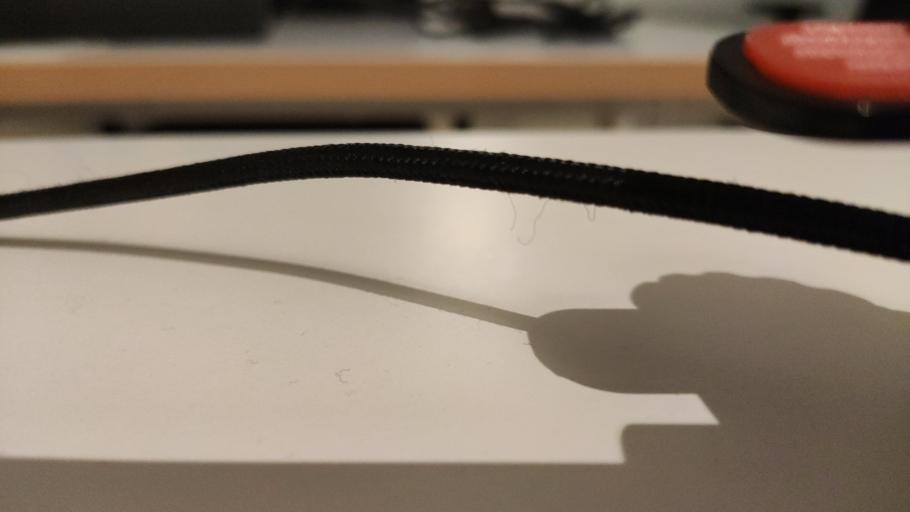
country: RU
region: Moskovskaya
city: Rogachevo
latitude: 56.4104
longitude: 37.2295
